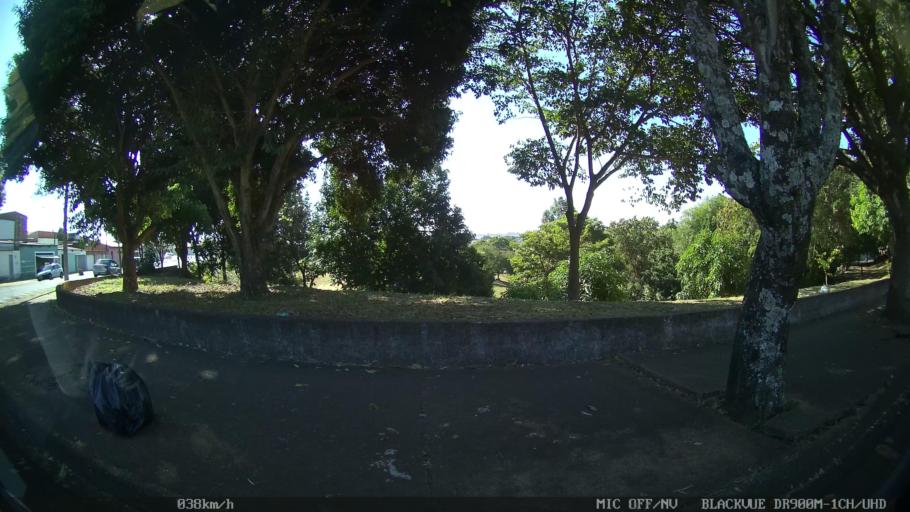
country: BR
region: Sao Paulo
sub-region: Franca
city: Franca
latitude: -20.4971
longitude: -47.4131
